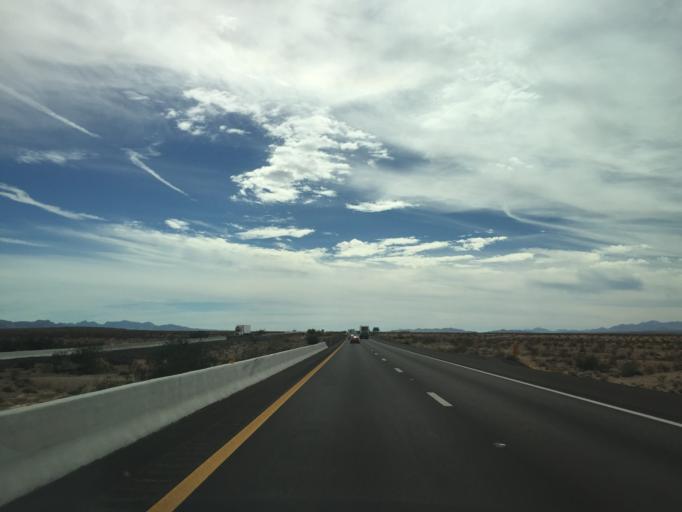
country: US
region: Nevada
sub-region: Clark County
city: Moapa Town
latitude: 36.5949
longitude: -114.6445
